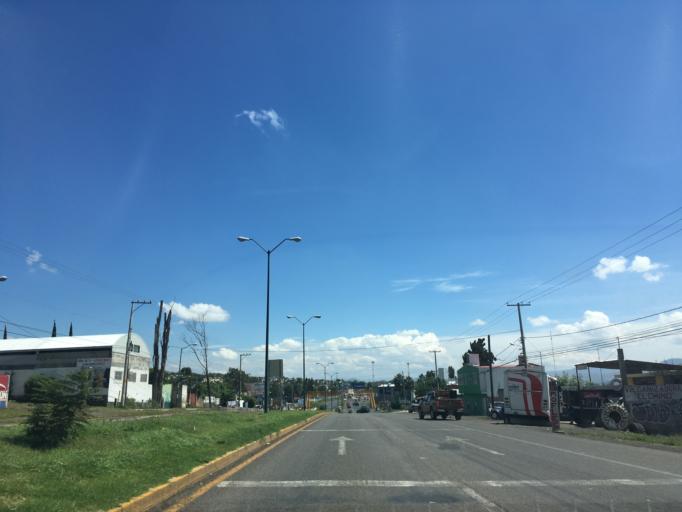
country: MX
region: Michoacan
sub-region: Morelia
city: Conjunto Habitacional Villas del Pedregal
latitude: 19.6875
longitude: -101.3069
